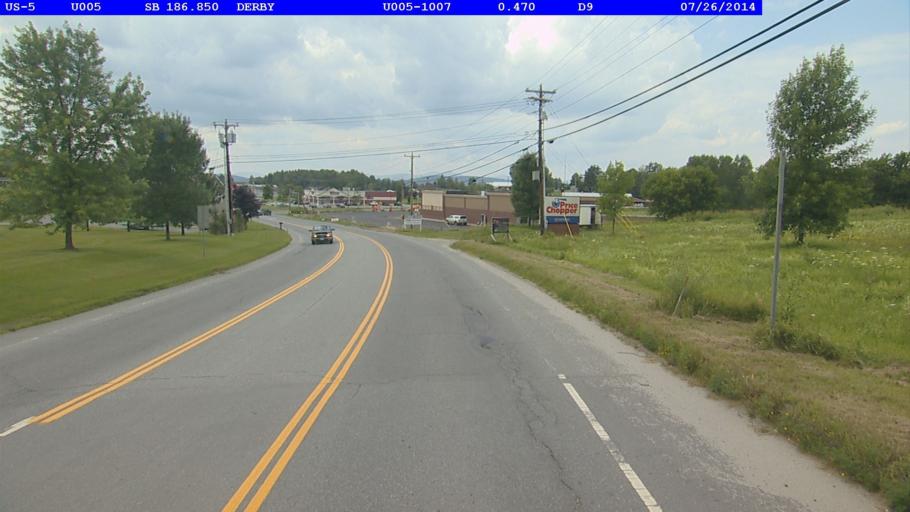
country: US
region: Vermont
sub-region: Orleans County
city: Newport
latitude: 44.9516
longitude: -72.1613
